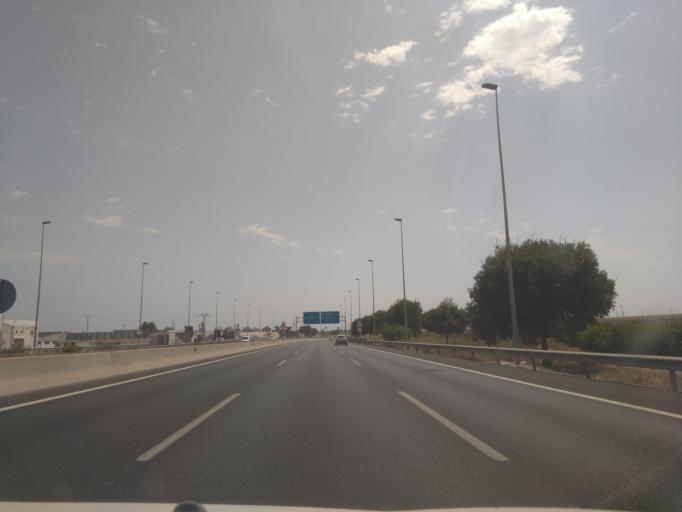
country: ES
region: Valencia
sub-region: Provincia de Valencia
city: Silla
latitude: 39.3563
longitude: -0.4259
